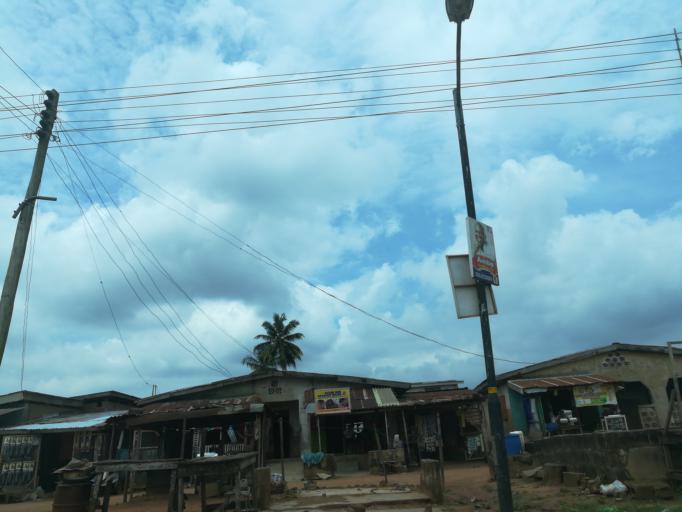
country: NG
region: Lagos
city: Ejirin
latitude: 6.6467
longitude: 3.7131
